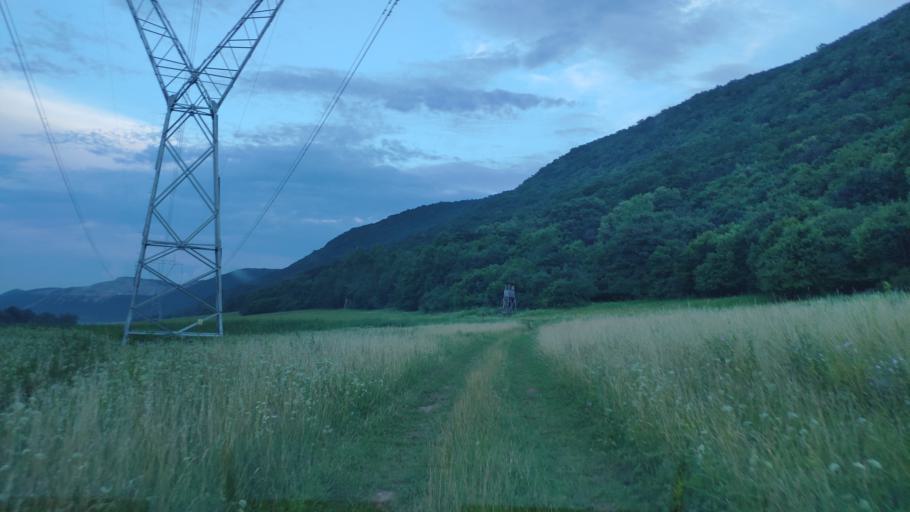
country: SK
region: Kosicky
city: Medzev
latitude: 48.5842
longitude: 20.7582
